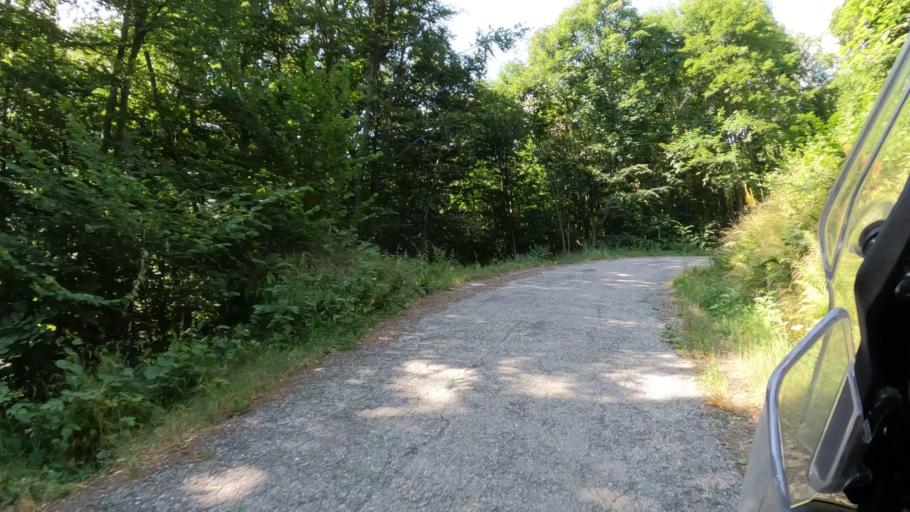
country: IT
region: Piedmont
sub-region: Provincia di Torino
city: Lemie
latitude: 45.2153
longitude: 7.3128
